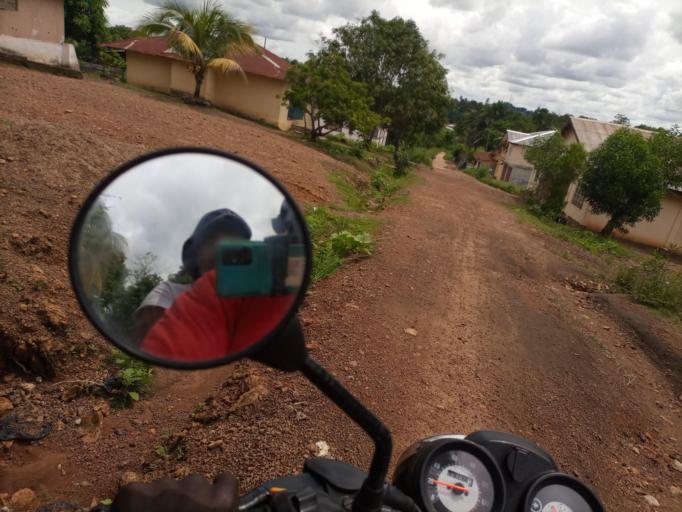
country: SL
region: Southern Province
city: Bo
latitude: 7.9735
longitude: -11.7222
